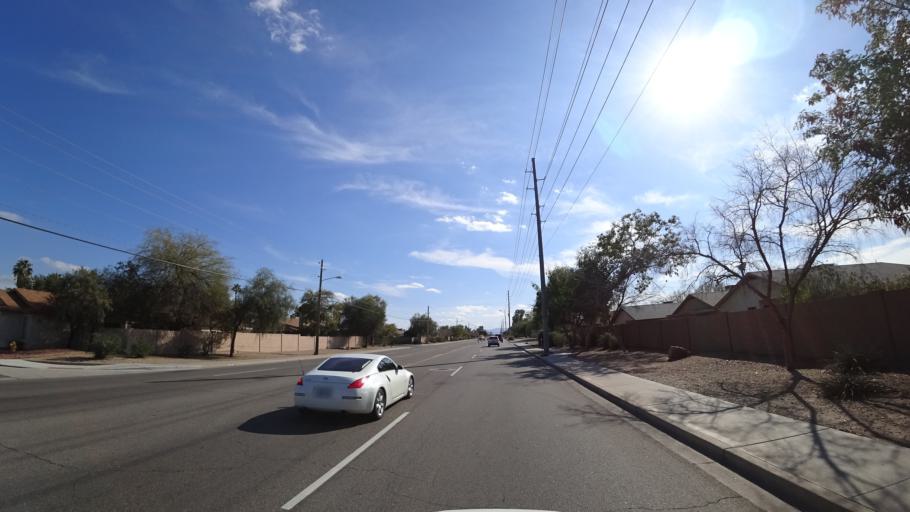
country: US
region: Arizona
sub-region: Maricopa County
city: Peoria
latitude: 33.5931
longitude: -112.2203
